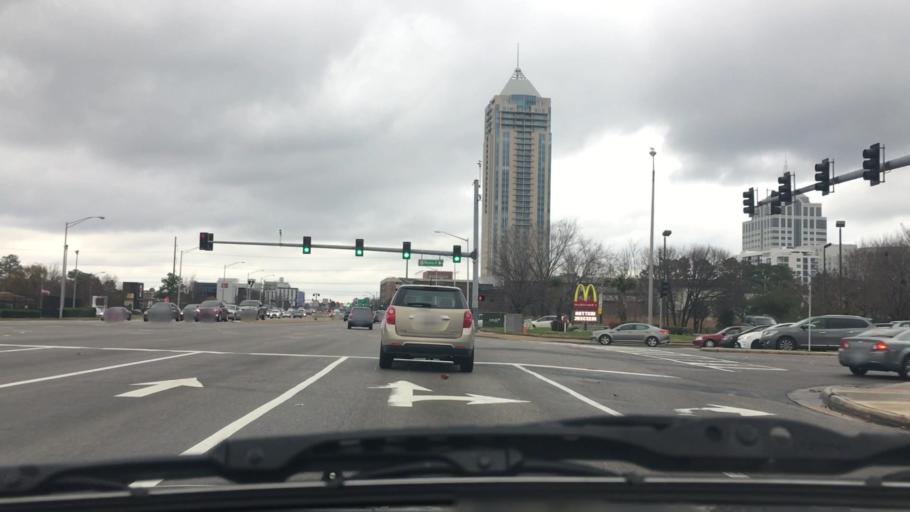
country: US
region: Virginia
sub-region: City of Chesapeake
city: Chesapeake
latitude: 36.8371
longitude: -76.1369
